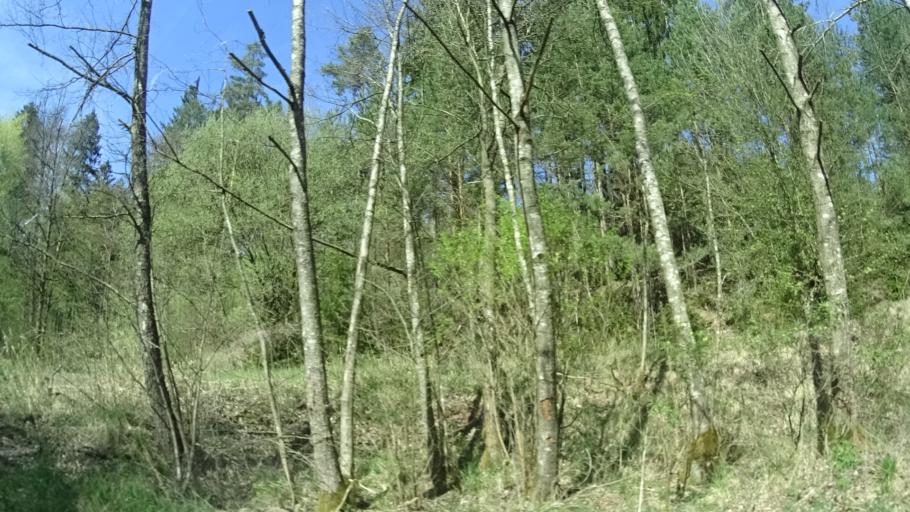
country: DE
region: Thuringia
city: Hellingen
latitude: 50.2862
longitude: 10.7716
